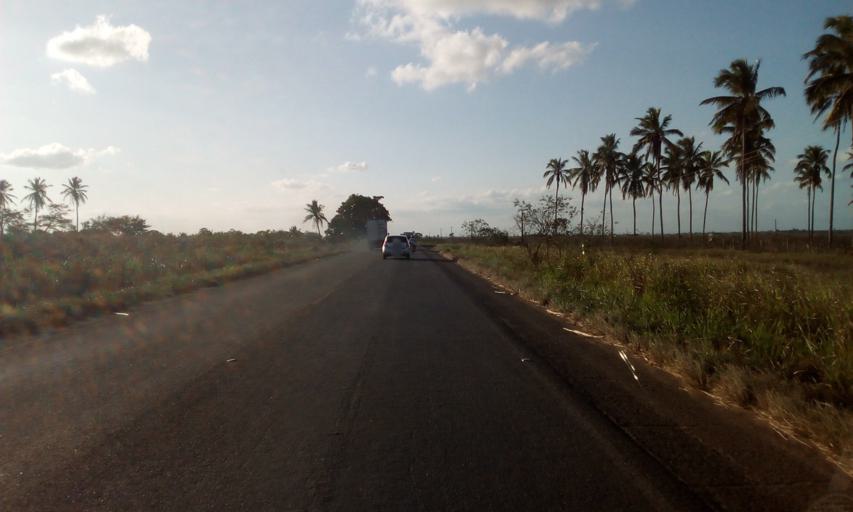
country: BR
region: Paraiba
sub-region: Mari
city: Mari
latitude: -7.0729
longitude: -35.2695
